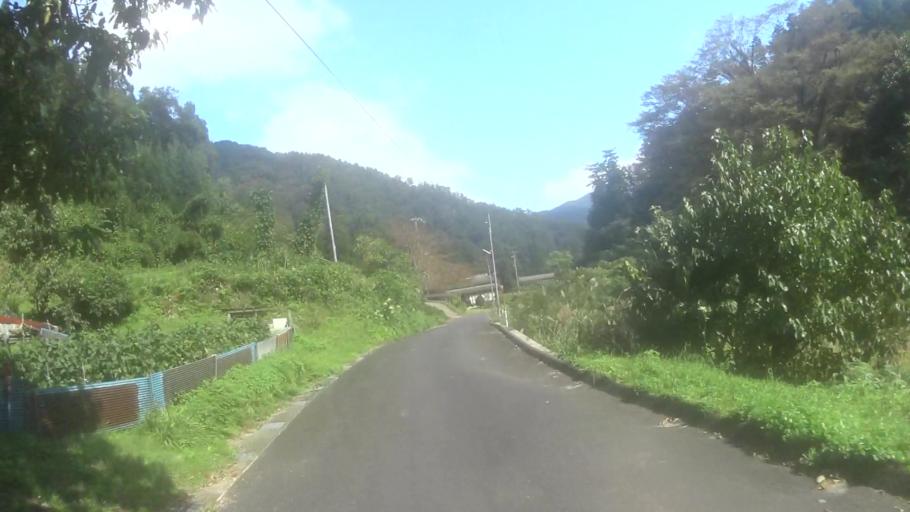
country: JP
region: Kyoto
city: Miyazu
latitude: 35.6732
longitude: 135.1462
